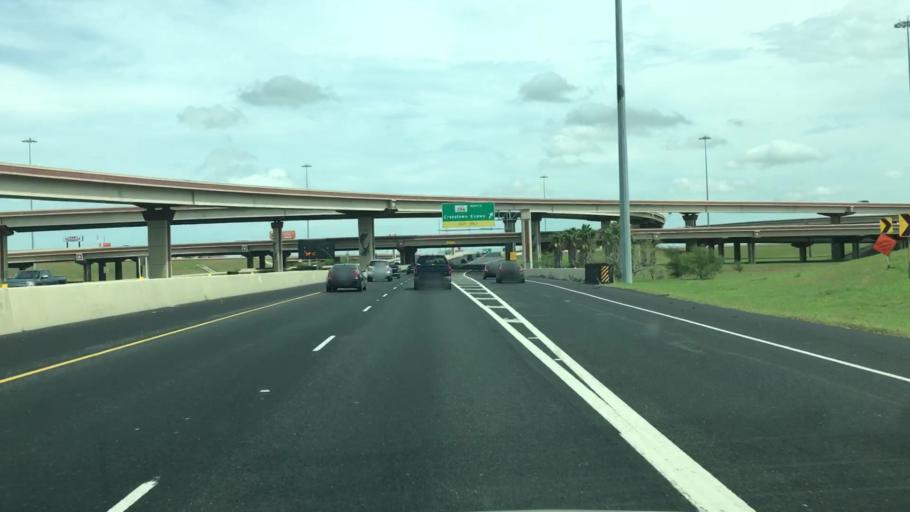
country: US
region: Texas
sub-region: Nueces County
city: Corpus Christi
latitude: 27.7381
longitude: -97.4326
